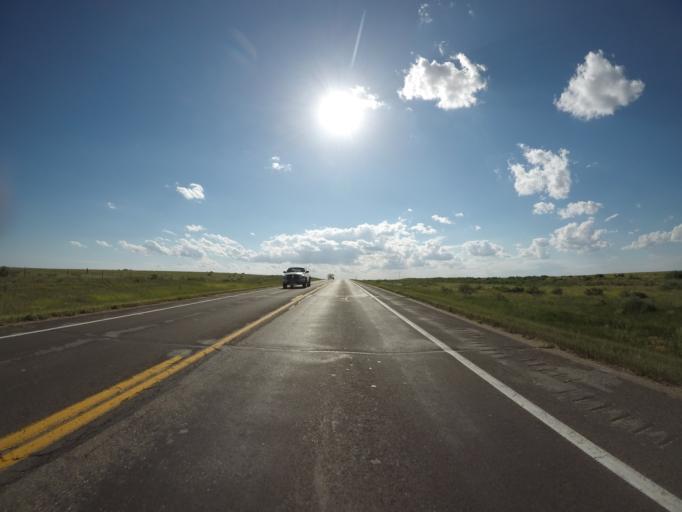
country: US
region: Colorado
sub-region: Morgan County
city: Fort Morgan
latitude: 40.5963
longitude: -103.8931
